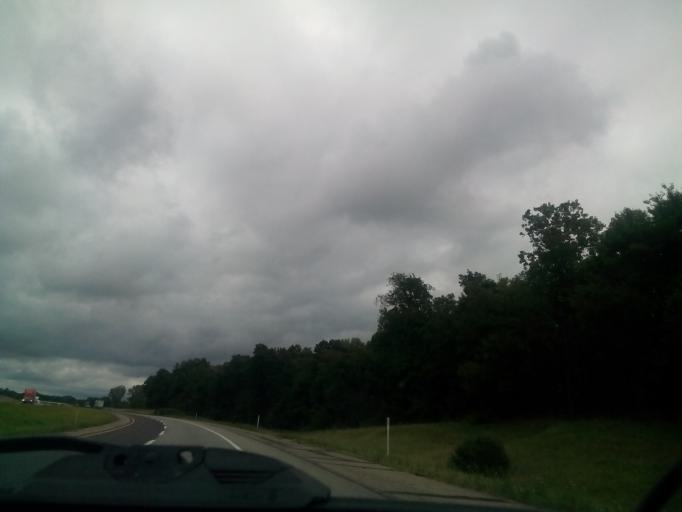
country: US
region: Michigan
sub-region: Saint Joseph County
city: Sturgis
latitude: 41.7413
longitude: -85.2777
